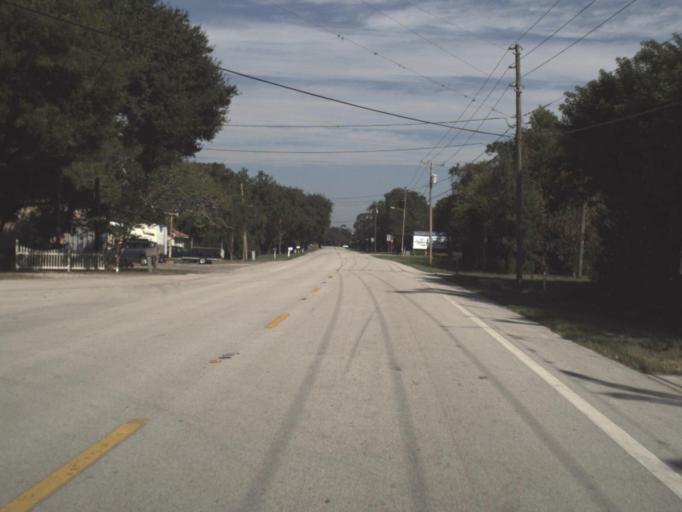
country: US
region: Florida
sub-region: Highlands County
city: Sebring
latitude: 27.5577
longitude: -81.4532
